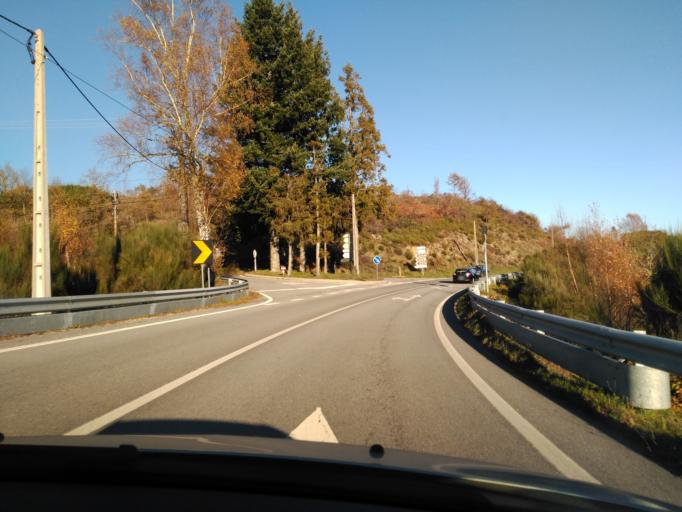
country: PT
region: Vila Real
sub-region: Montalegre
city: Montalegre
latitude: 41.7528
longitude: -7.8717
